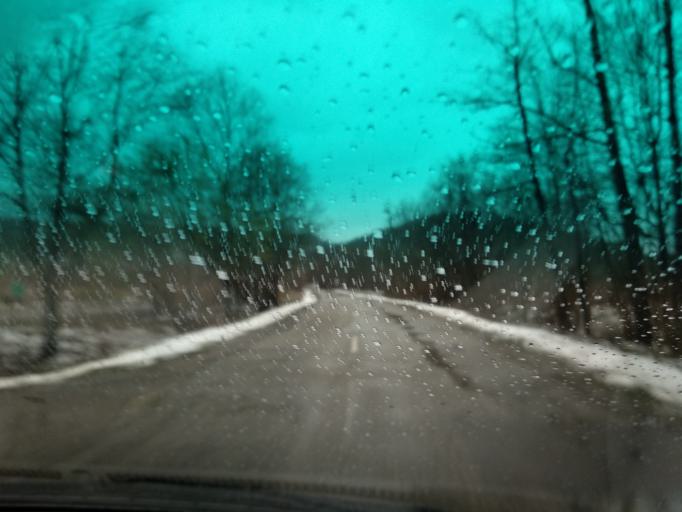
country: RU
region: Krasnodarskiy
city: Khadyzhensk
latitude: 44.2199
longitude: 39.3948
